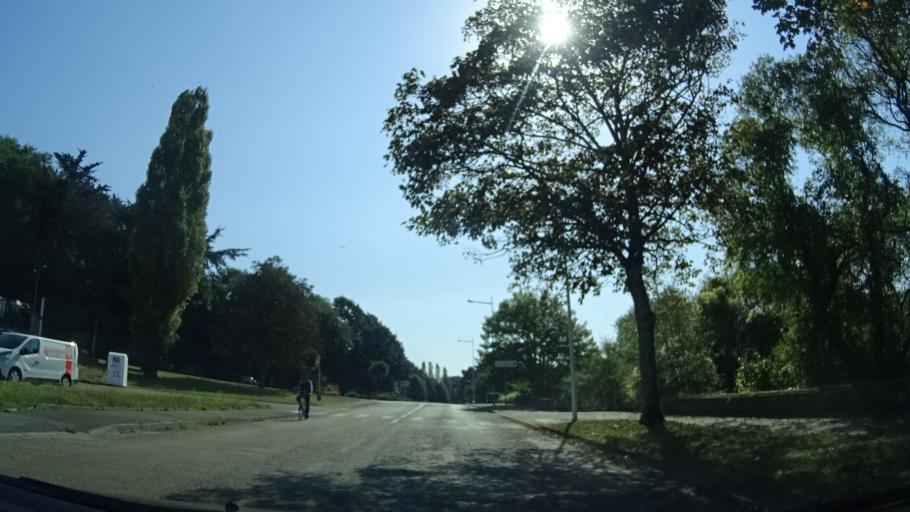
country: FR
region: Brittany
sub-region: Departement du Finistere
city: Douarnenez
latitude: 48.0829
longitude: -4.3300
